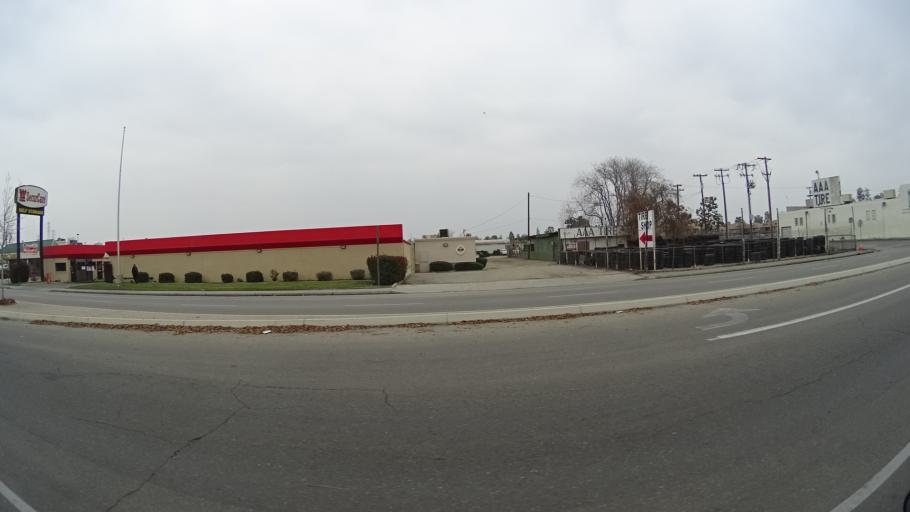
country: US
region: California
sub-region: Kern County
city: Oildale
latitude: 35.3967
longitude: -119.0188
